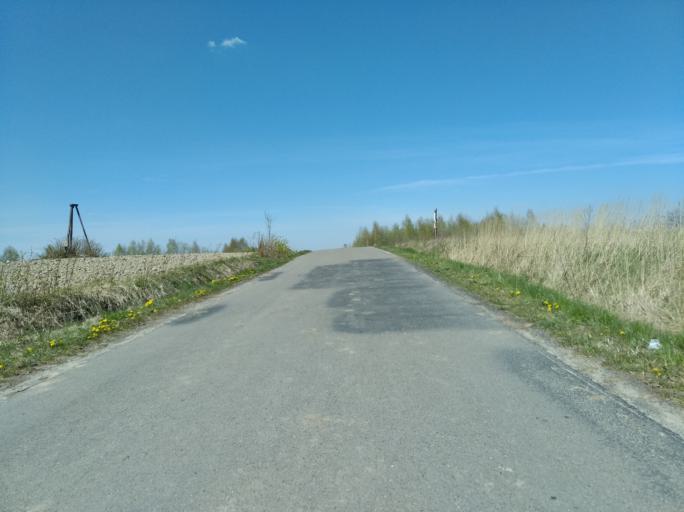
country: PL
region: Subcarpathian Voivodeship
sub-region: Powiat brzozowski
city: Jablonka
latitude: 49.7345
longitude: 22.1172
